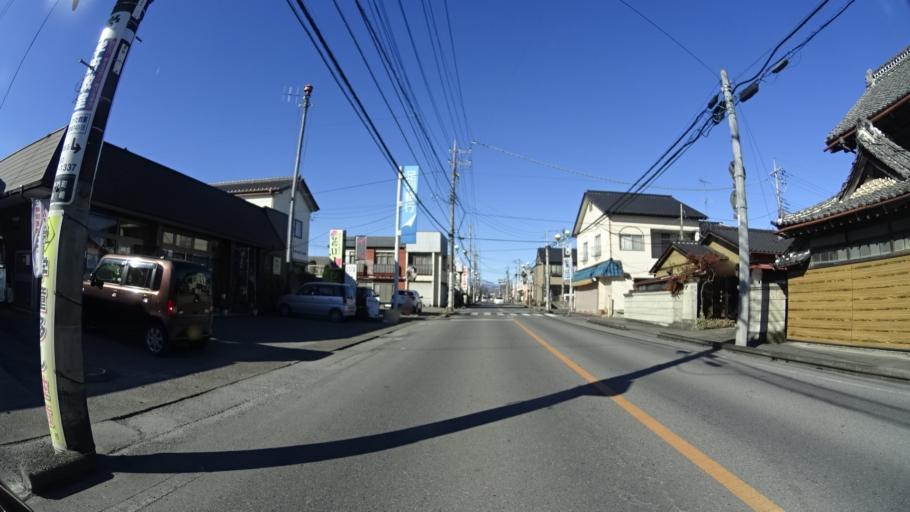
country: JP
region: Tochigi
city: Mibu
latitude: 36.4677
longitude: 139.7503
